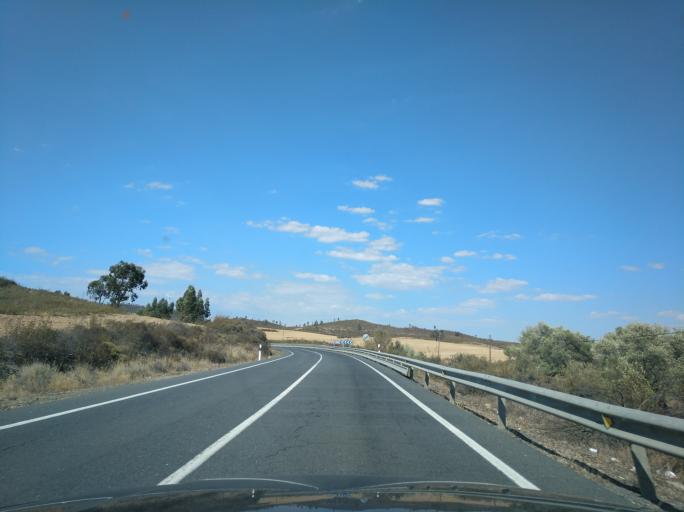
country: ES
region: Andalusia
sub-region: Provincia de Huelva
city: Alosno
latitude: 37.5692
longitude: -7.1175
